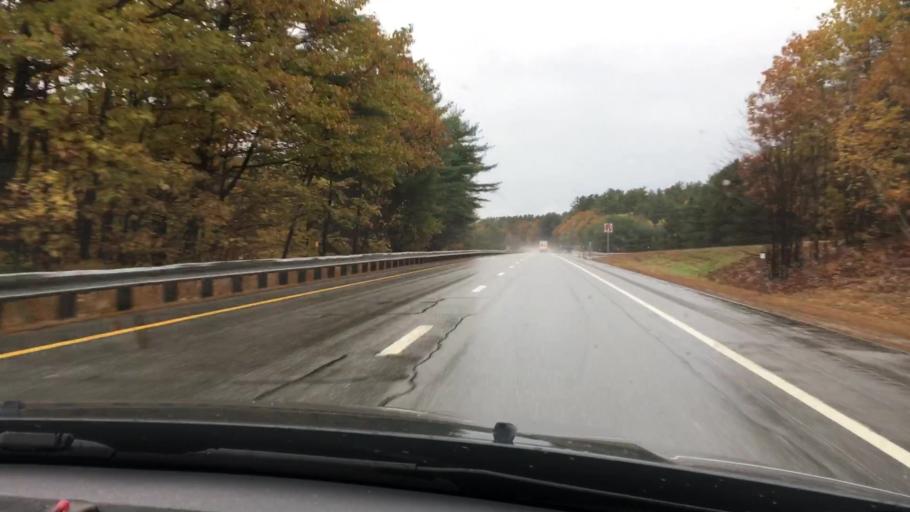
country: US
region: New Hampshire
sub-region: Grafton County
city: Ashland
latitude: 43.6149
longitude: -71.6433
